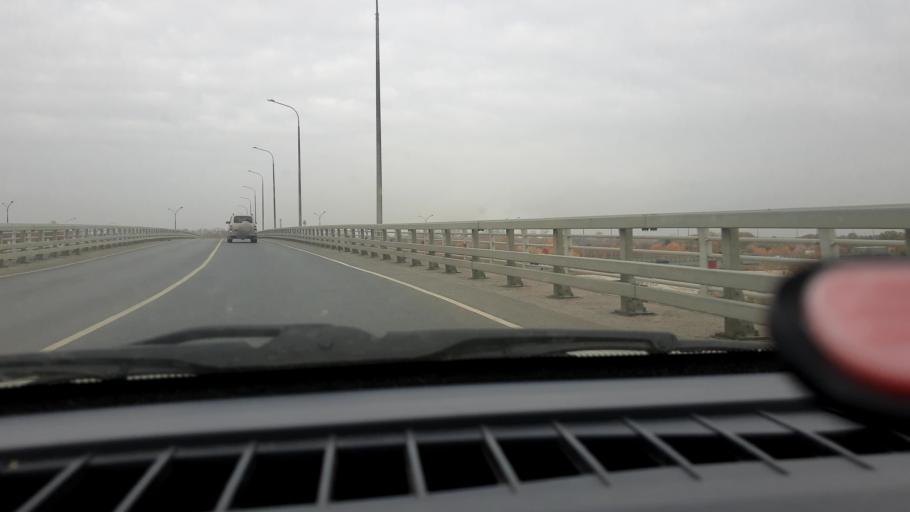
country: RU
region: Nizjnij Novgorod
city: Neklyudovo
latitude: 56.3953
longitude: 43.9902
